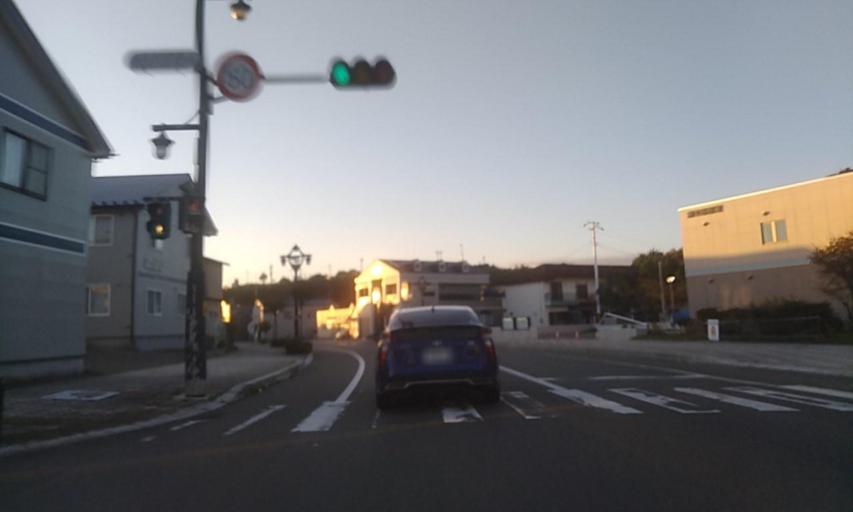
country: JP
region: Hokkaido
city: Shizunai-furukawacho
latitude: 42.1598
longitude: 142.7812
